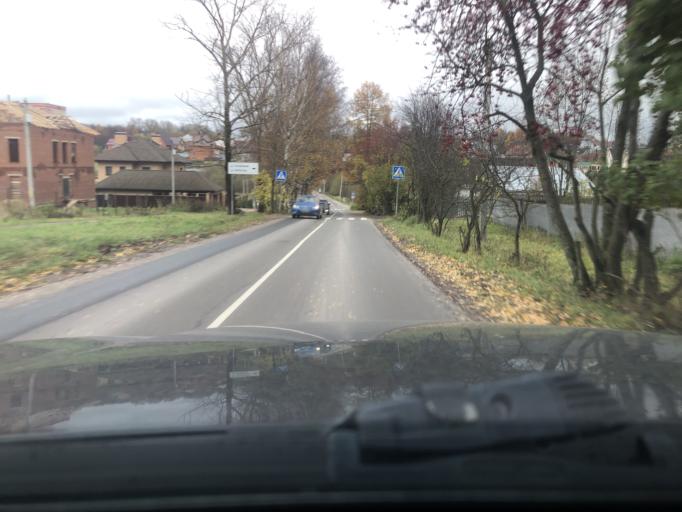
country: RU
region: Moskovskaya
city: Sergiyev Posad
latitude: 56.3016
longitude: 38.1103
